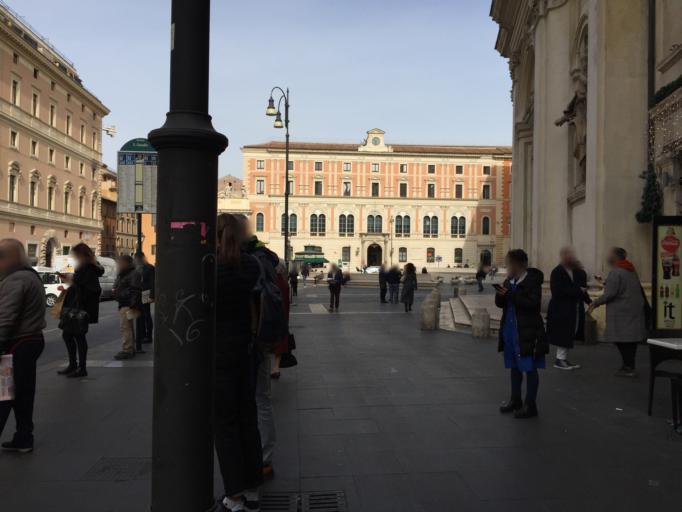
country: VA
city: Vatican City
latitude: 41.9020
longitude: 12.4816
